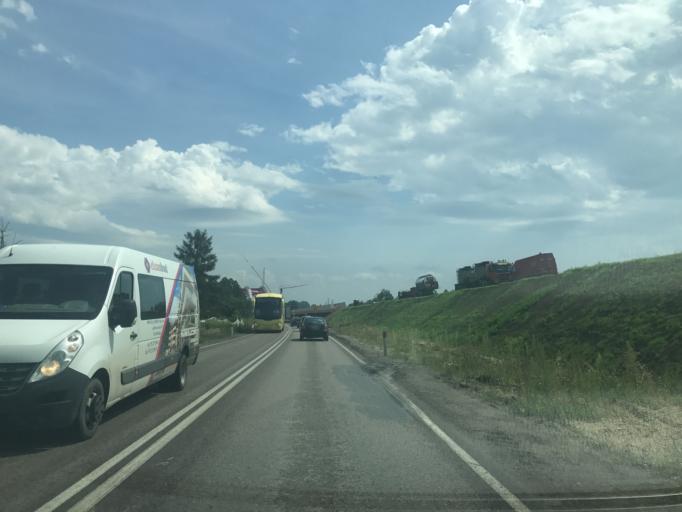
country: PL
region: Warmian-Masurian Voivodeship
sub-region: Powiat ostrodzki
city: Ostroda
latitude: 53.7166
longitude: 19.9556
